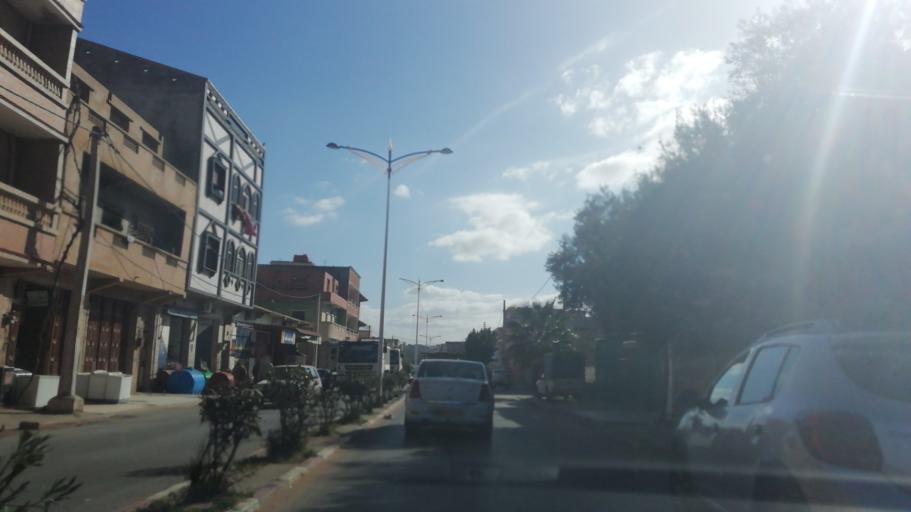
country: DZ
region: Mostaganem
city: Mostaganem
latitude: 35.9985
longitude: 0.3047
